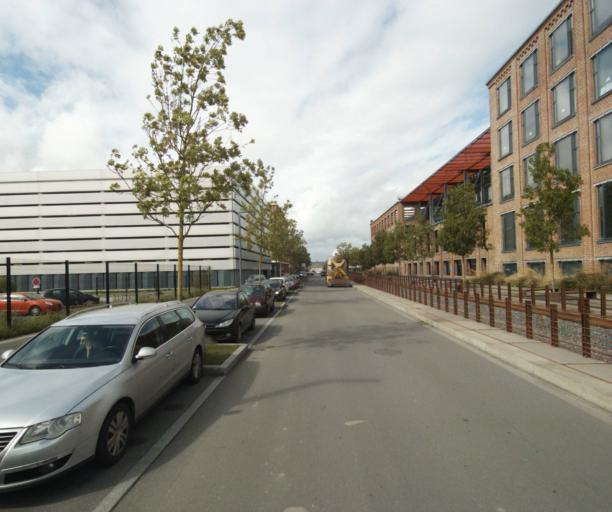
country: FR
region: Nord-Pas-de-Calais
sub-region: Departement du Nord
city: Lambersart
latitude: 50.6324
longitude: 3.0200
